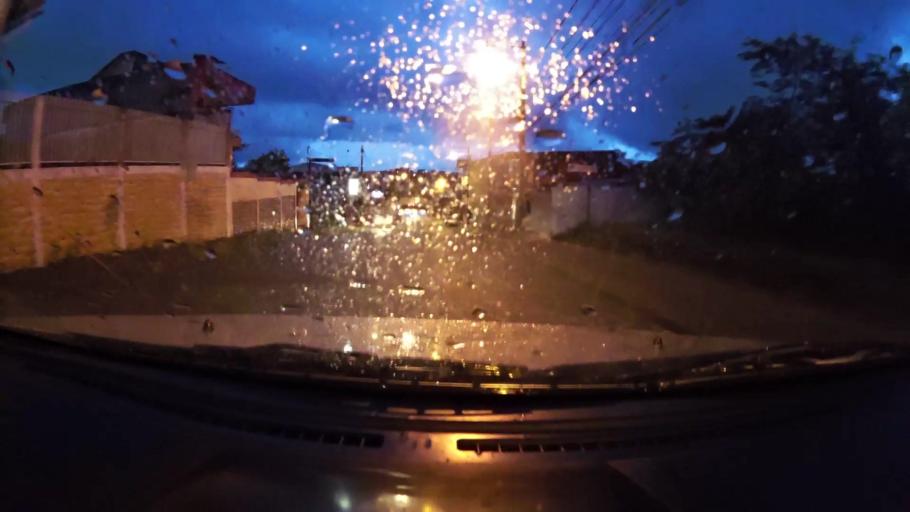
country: EC
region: Pastaza
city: Puyo
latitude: -1.4840
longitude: -78.0021
